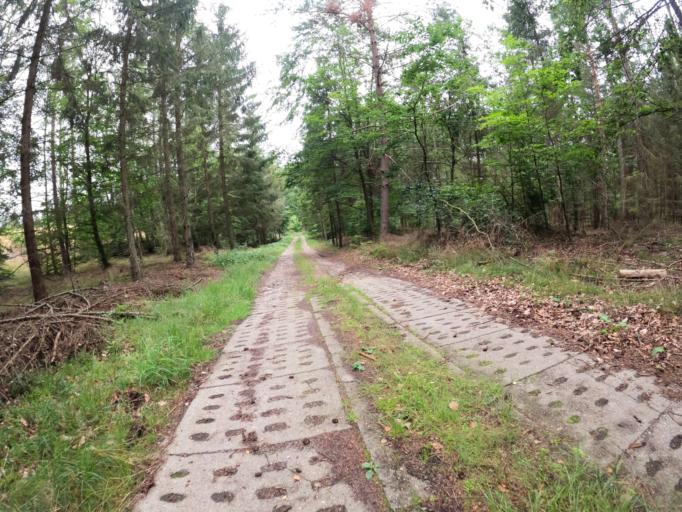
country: PL
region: West Pomeranian Voivodeship
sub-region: Powiat szczecinecki
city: Grzmiaca
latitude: 53.9773
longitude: 16.4086
